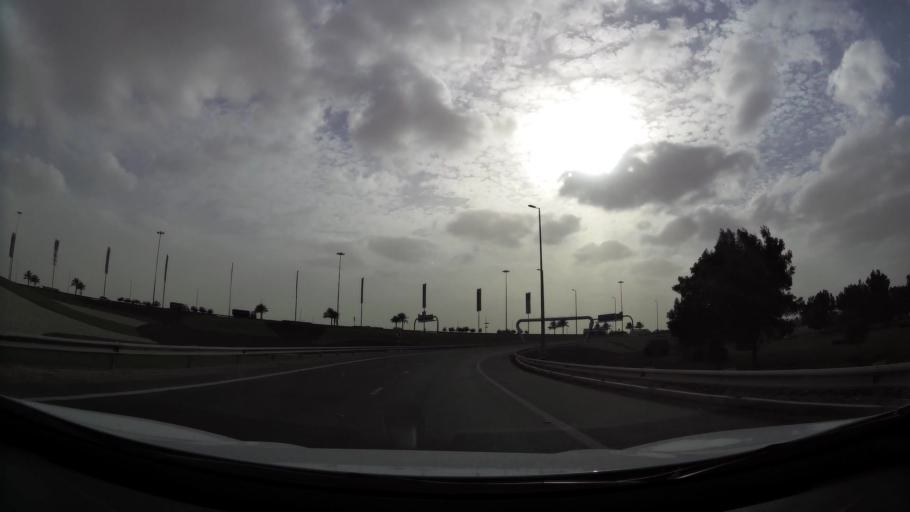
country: AE
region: Abu Dhabi
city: Abu Dhabi
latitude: 24.4905
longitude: 54.6283
